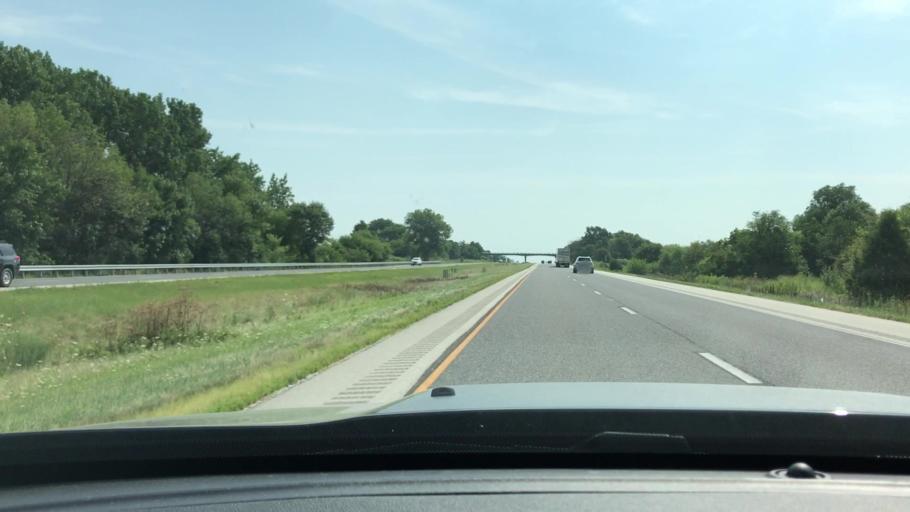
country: US
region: Illinois
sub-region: Henry County
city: Geneseo
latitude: 41.4404
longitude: -90.2381
